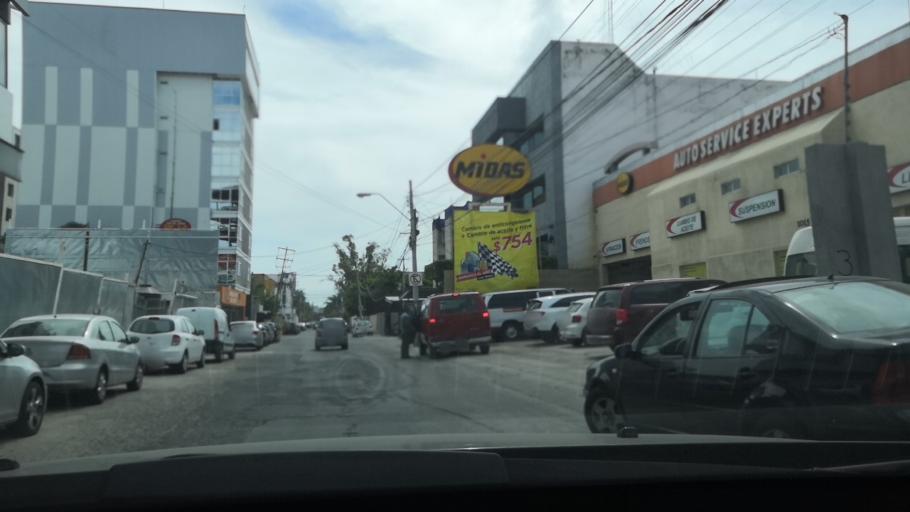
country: MX
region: Guanajuato
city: Leon
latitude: 21.1562
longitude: -101.6917
